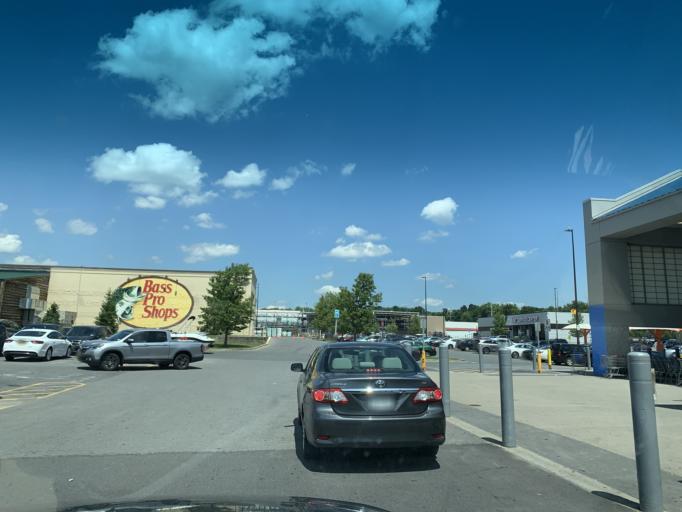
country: US
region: New York
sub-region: Oneida County
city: Utica
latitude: 43.1242
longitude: -75.2259
